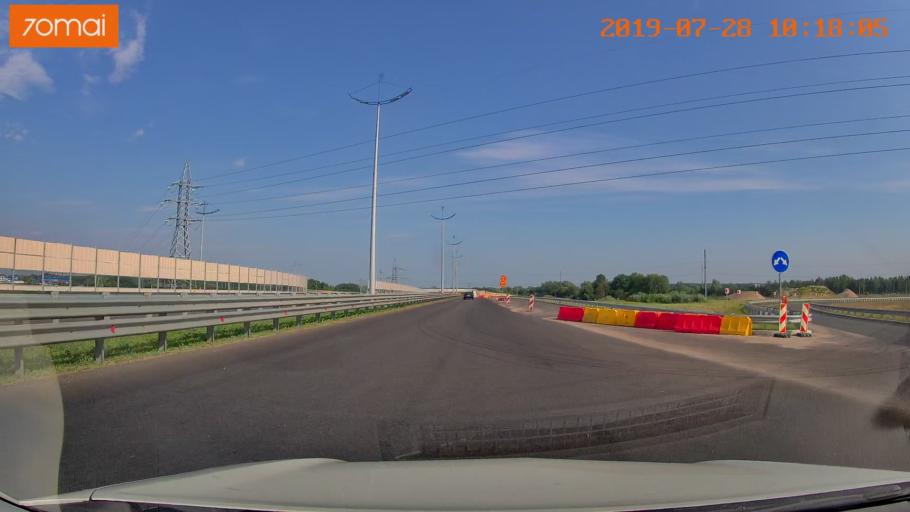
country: RU
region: Kaliningrad
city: Maloye Isakovo
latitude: 54.7474
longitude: 20.5909
